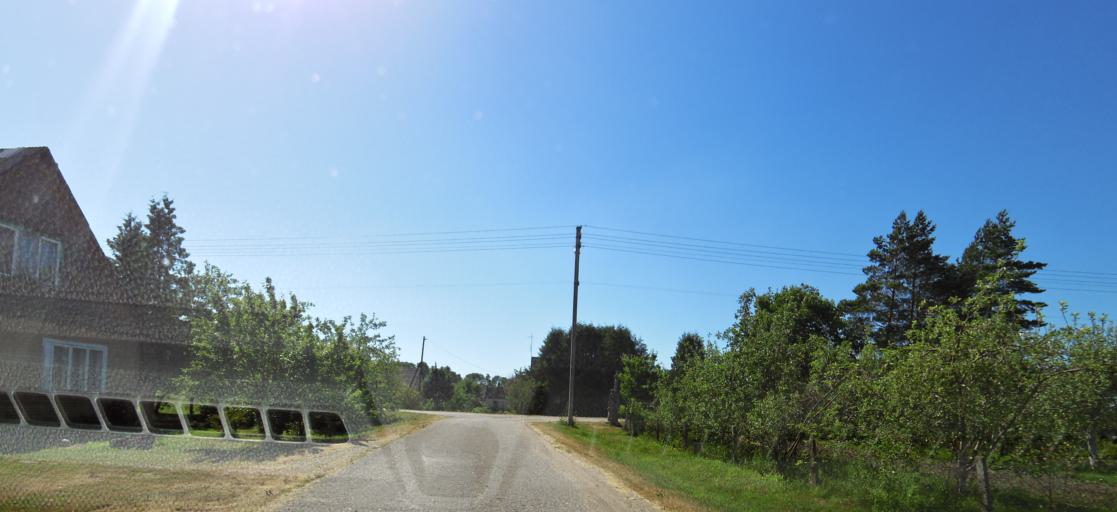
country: LT
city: Vabalninkas
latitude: 55.9754
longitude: 24.6631
